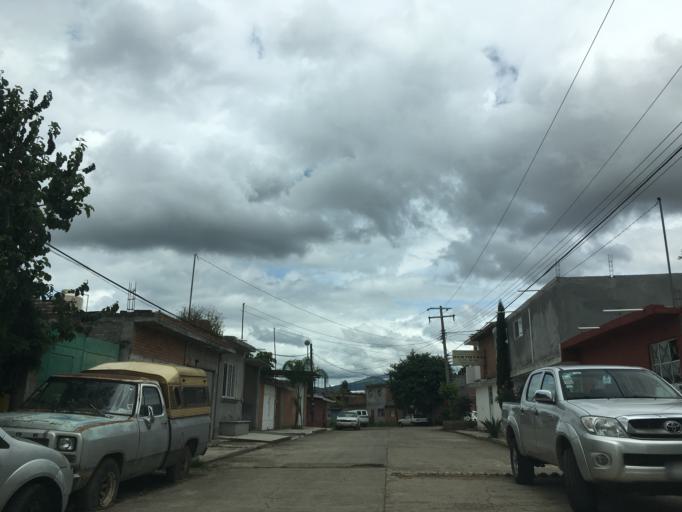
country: MX
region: Michoacan
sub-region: Morelia
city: Morelos
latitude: 19.6493
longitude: -101.2327
